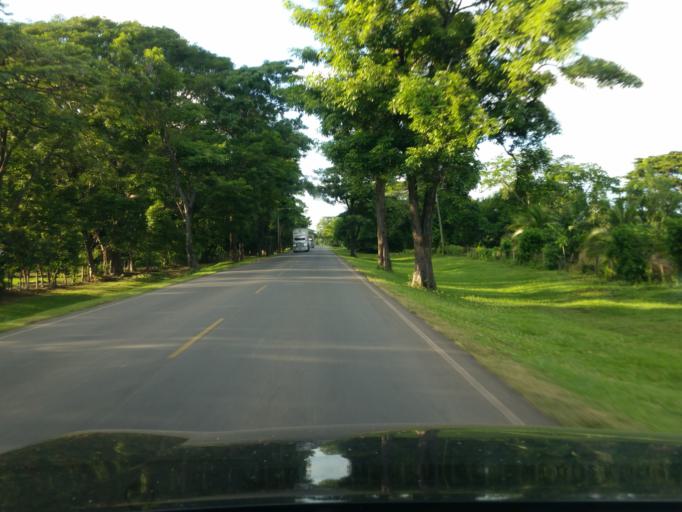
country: NI
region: Granada
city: Nandaime
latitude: 11.7401
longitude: -86.0220
